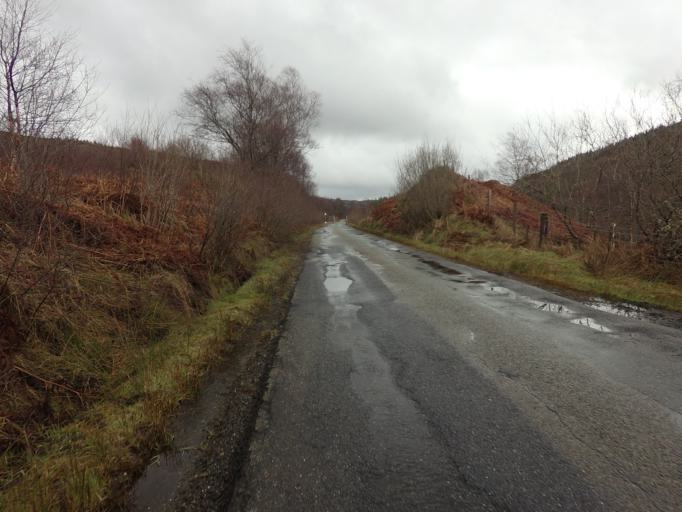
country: GB
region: Scotland
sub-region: West Dunbartonshire
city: Balloch
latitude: 56.2445
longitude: -4.5753
